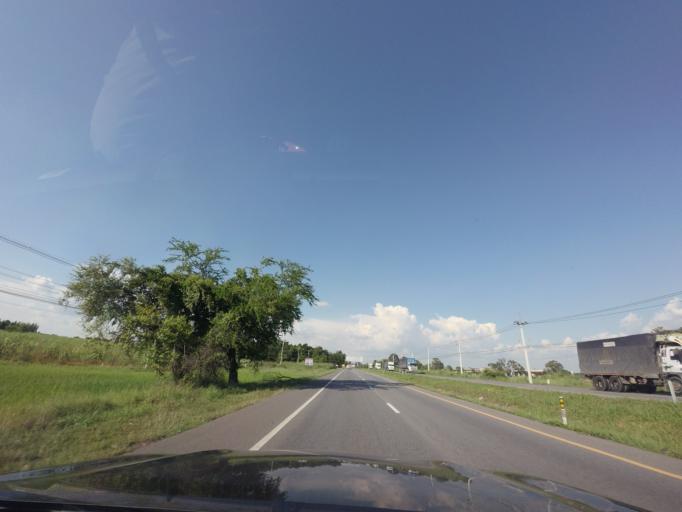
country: TH
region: Khon Kaen
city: Non Sila
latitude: 15.9560
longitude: 102.6864
